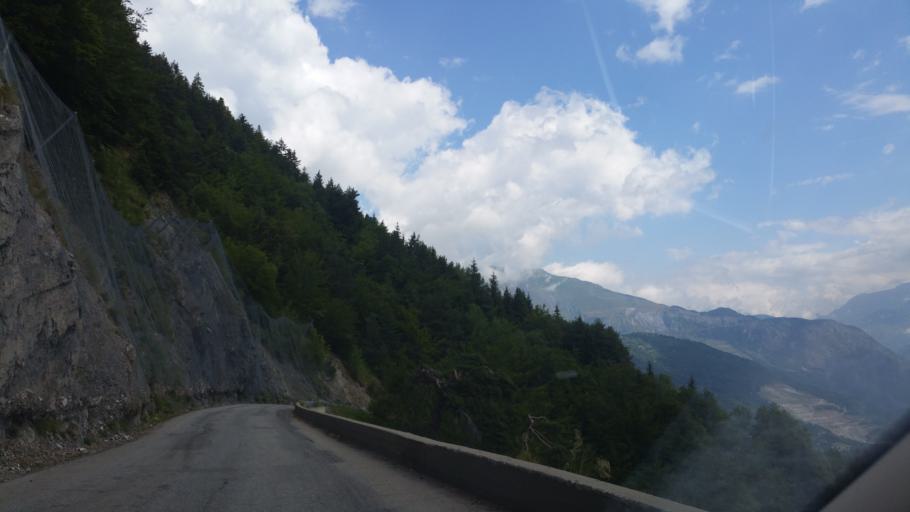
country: FR
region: Rhone-Alpes
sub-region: Departement de la Savoie
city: Saint-Jean-de-Maurienne
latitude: 45.2240
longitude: 6.3041
